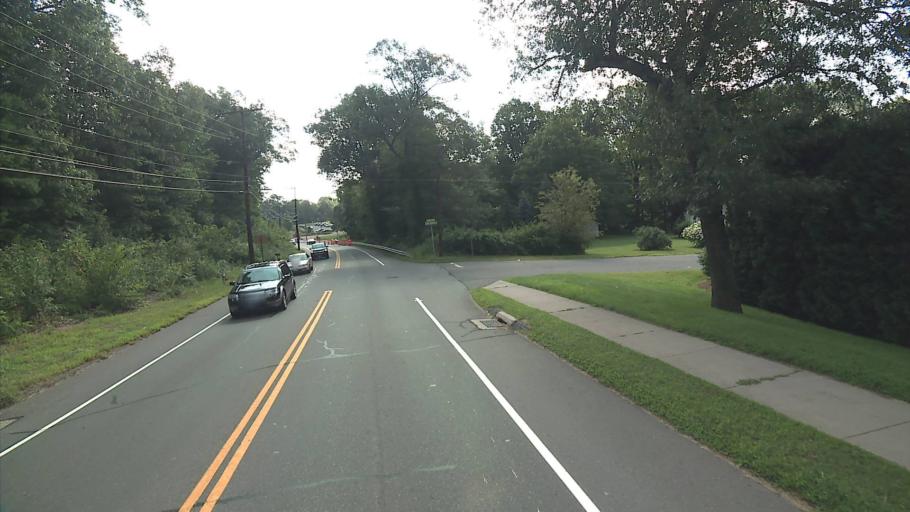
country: US
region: Connecticut
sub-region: Hartford County
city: Hazardville
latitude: 41.9845
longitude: -72.5218
